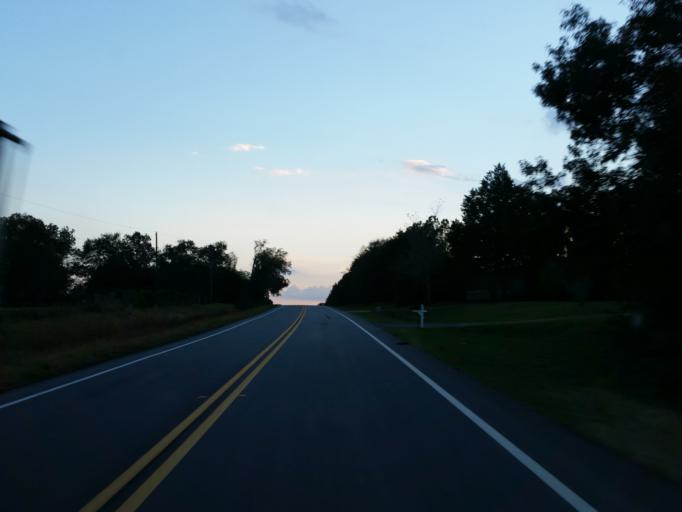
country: US
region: Georgia
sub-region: Pulaski County
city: Hawkinsville
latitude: 32.2524
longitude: -83.4944
